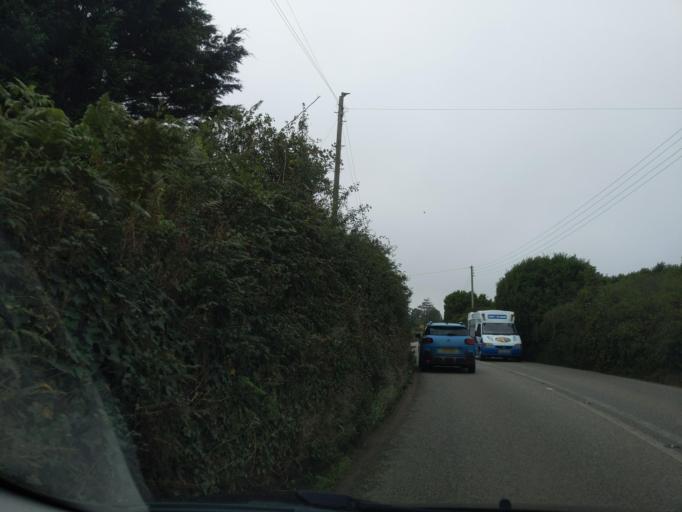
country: GB
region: England
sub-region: Cornwall
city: Germoe
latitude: 50.1076
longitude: -5.3470
